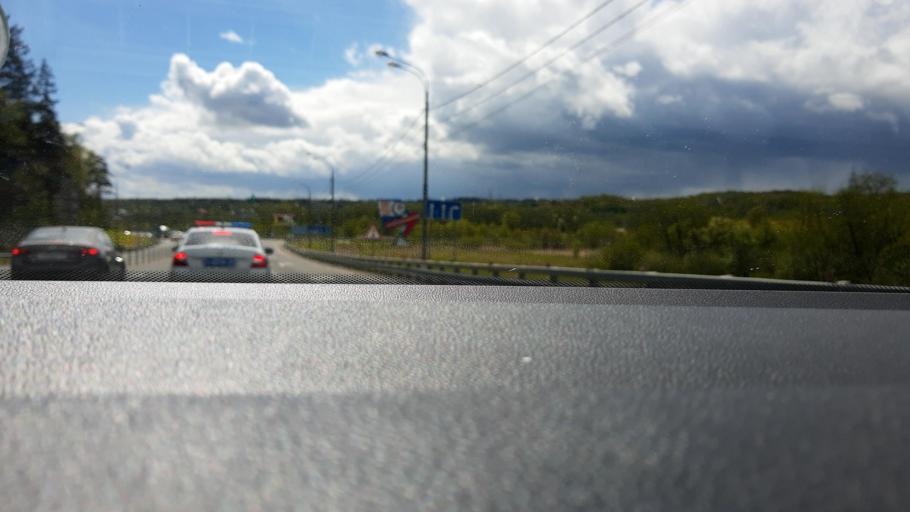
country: RU
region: Moskovskaya
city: Dedenevo
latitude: 56.2201
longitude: 37.5231
